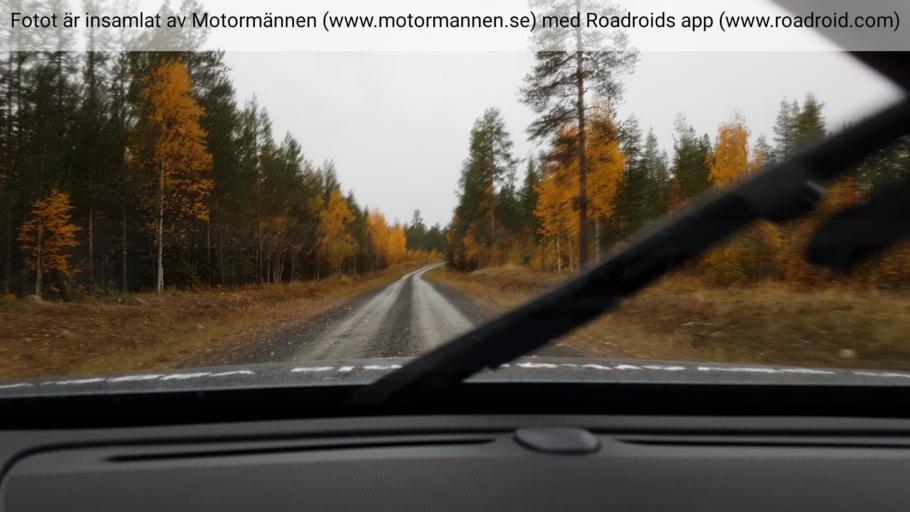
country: SE
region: Norrbotten
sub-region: Pajala Kommun
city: Pajala
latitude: 66.9971
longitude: 22.8635
